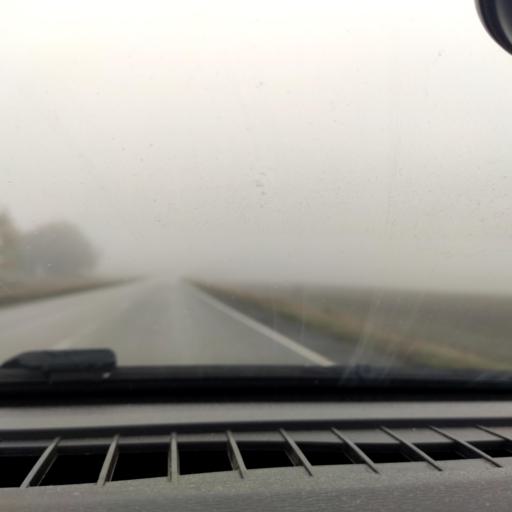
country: RU
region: Belgorod
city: Ilovka
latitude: 50.7652
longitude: 38.7475
